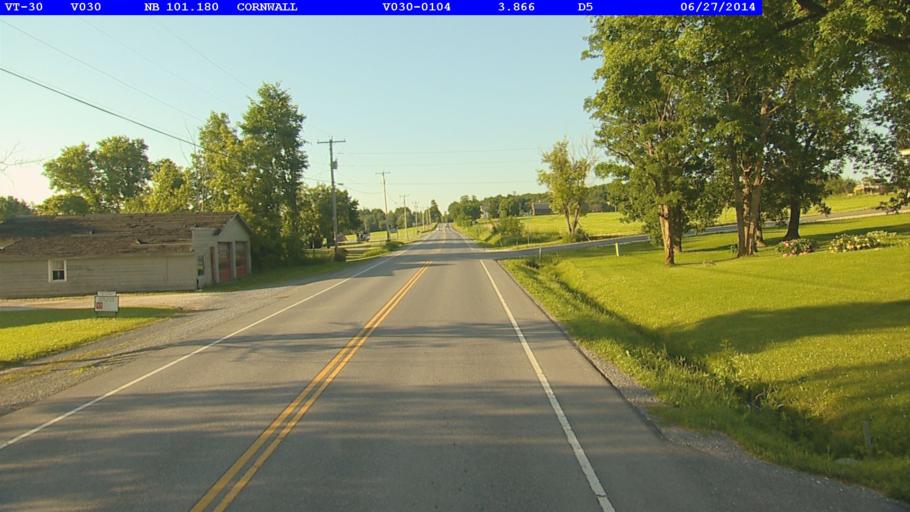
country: US
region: Vermont
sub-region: Addison County
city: Middlebury (village)
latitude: 43.9633
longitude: -73.2088
